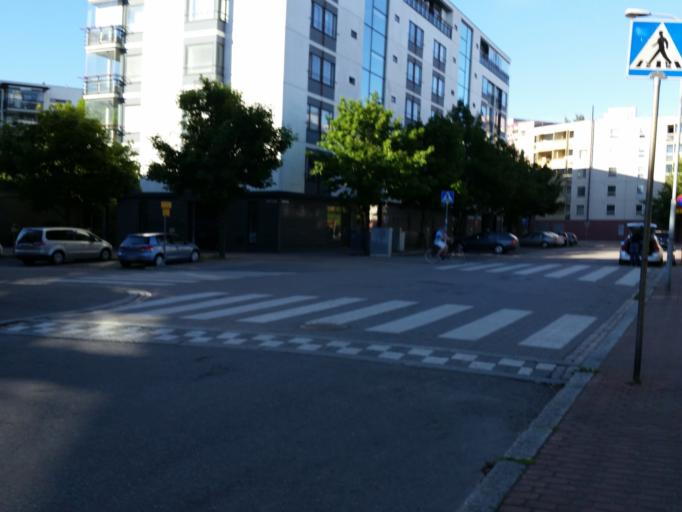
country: FI
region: Uusimaa
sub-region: Helsinki
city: Helsinki
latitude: 60.1605
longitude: 24.9145
